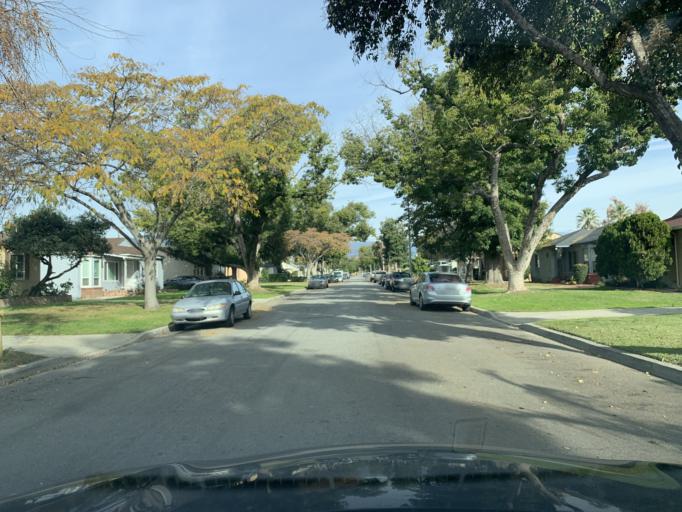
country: US
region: California
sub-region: Los Angeles County
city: West Covina
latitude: 34.0742
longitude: -117.9333
